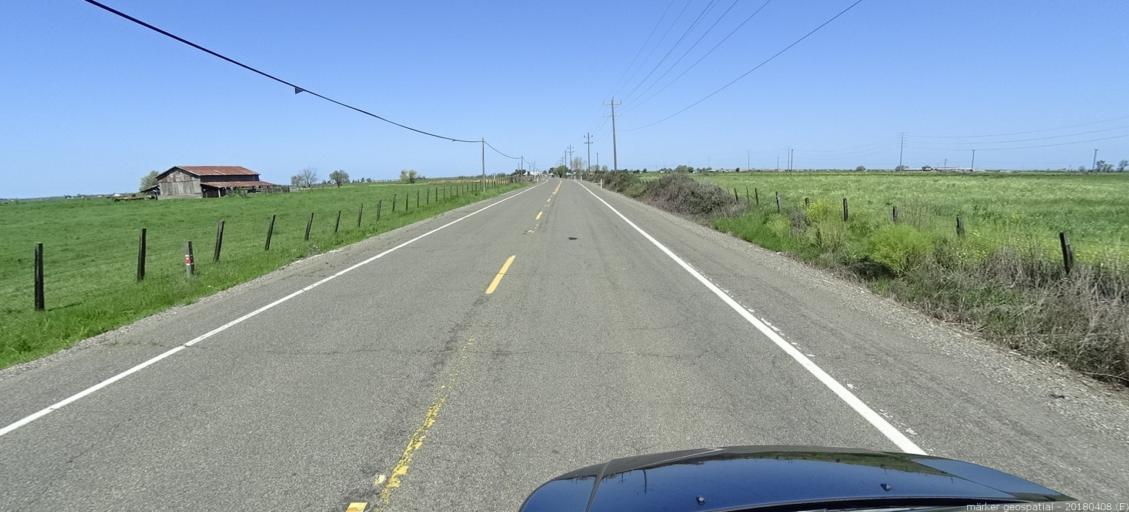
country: US
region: California
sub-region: Sacramento County
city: Laguna
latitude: 38.3553
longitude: -121.4518
